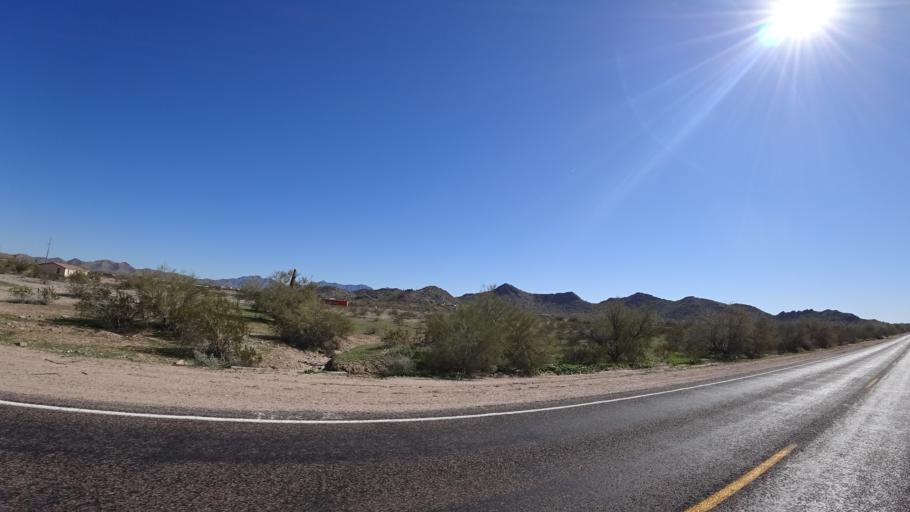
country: US
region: Arizona
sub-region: Maricopa County
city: Buckeye
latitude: 33.3242
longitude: -112.4698
